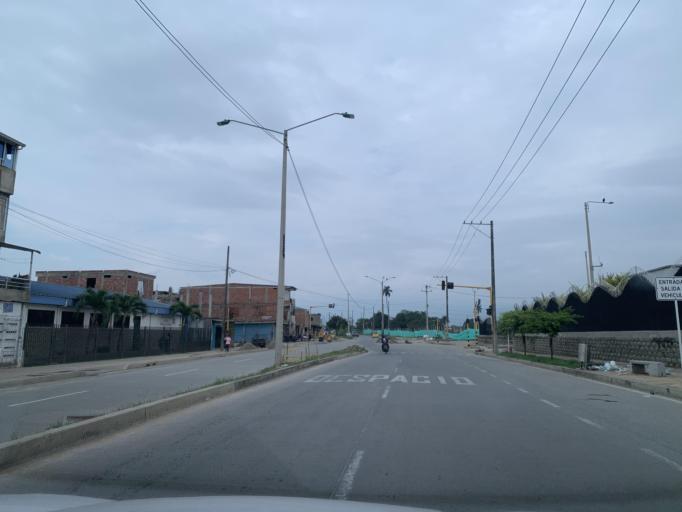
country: CO
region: Valle del Cauca
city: Cali
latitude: 3.4106
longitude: -76.4767
